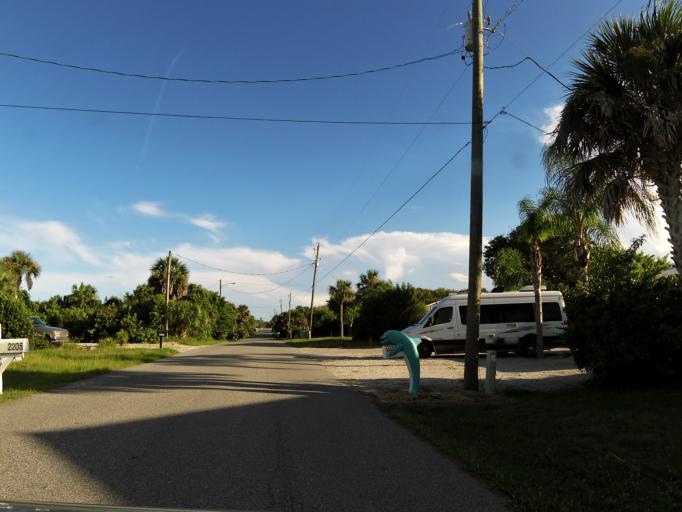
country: US
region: Florida
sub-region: Flagler County
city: Flagler Beach
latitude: 29.4559
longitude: -81.1178
